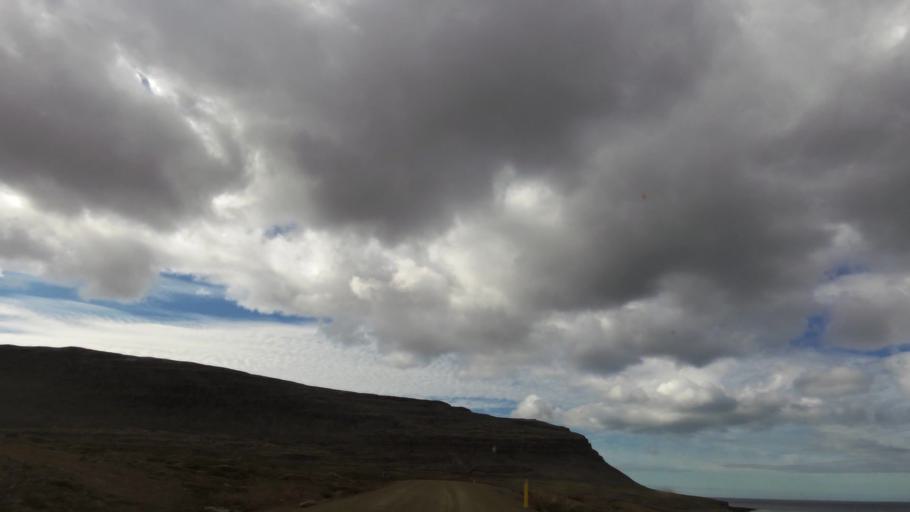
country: IS
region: West
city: Olafsvik
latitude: 65.5683
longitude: -24.0528
